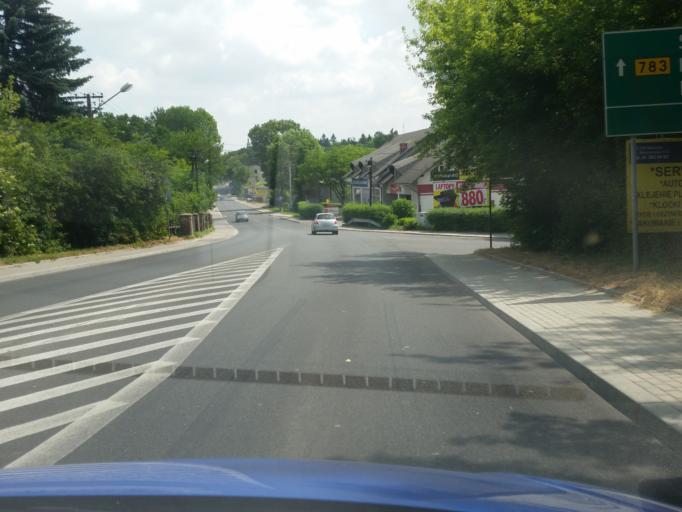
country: PL
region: Lesser Poland Voivodeship
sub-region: Powiat miechowski
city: Miechow
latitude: 50.3566
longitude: 20.0131
